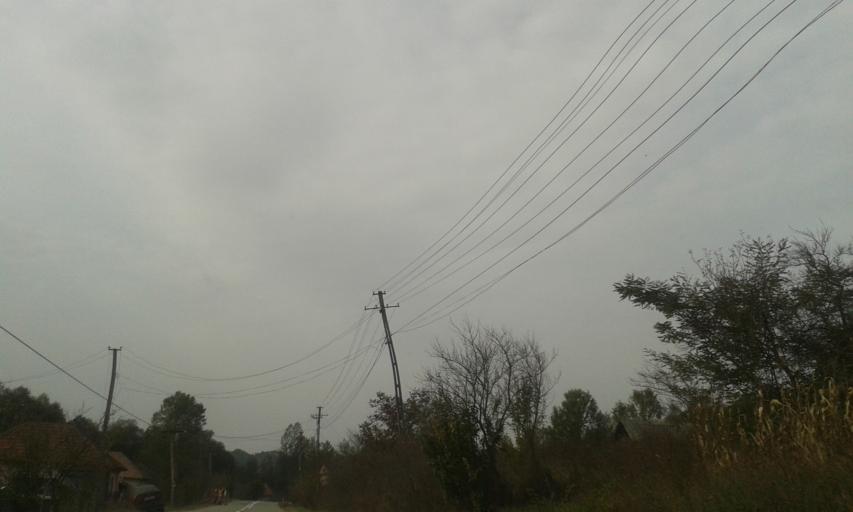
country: RO
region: Valcea
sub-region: Comuna Gradistea
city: Gradistea
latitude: 44.9044
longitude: 23.7977
